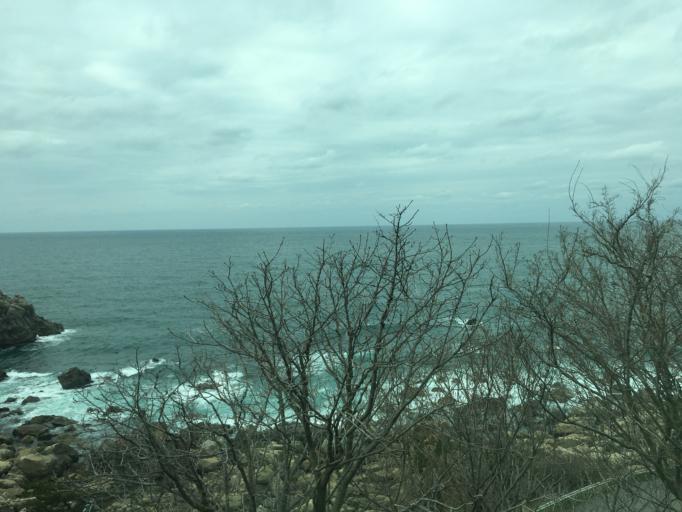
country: JP
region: Akita
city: Noshiromachi
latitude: 40.4416
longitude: 139.9409
